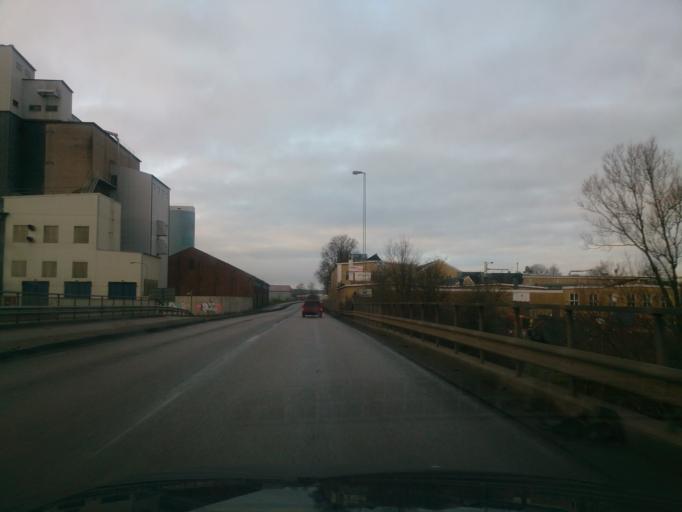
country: SE
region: OEstergoetland
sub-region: Linkopings Kommun
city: Linkoping
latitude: 58.4228
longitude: 15.6309
